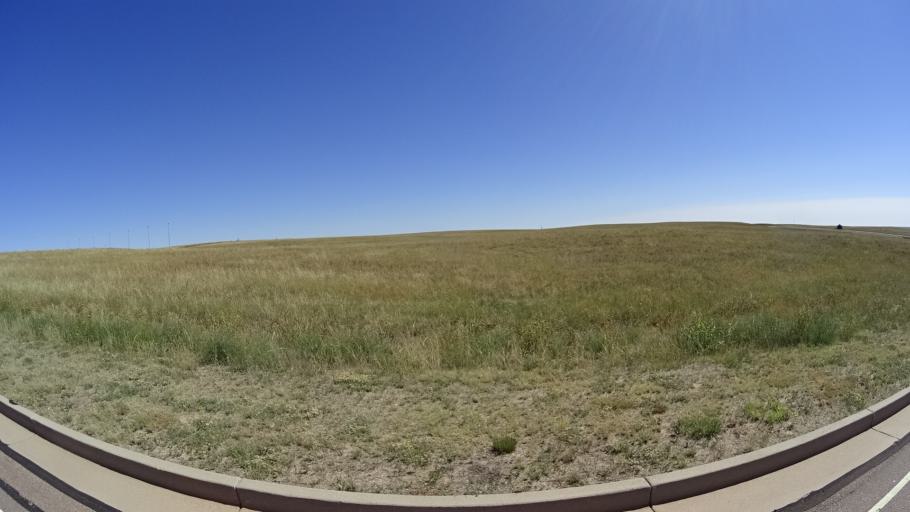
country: US
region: Colorado
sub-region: El Paso County
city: Security-Widefield
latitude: 38.7696
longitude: -104.6989
